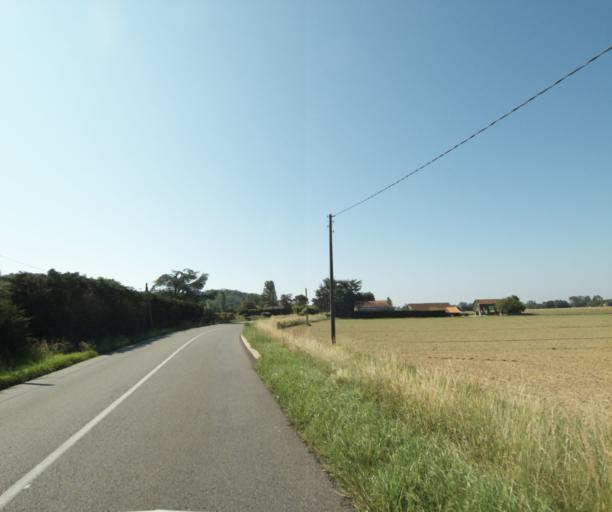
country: FR
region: Midi-Pyrenees
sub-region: Departement du Tarn-et-Garonne
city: Corbarieu
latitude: 43.9612
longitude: 1.3619
